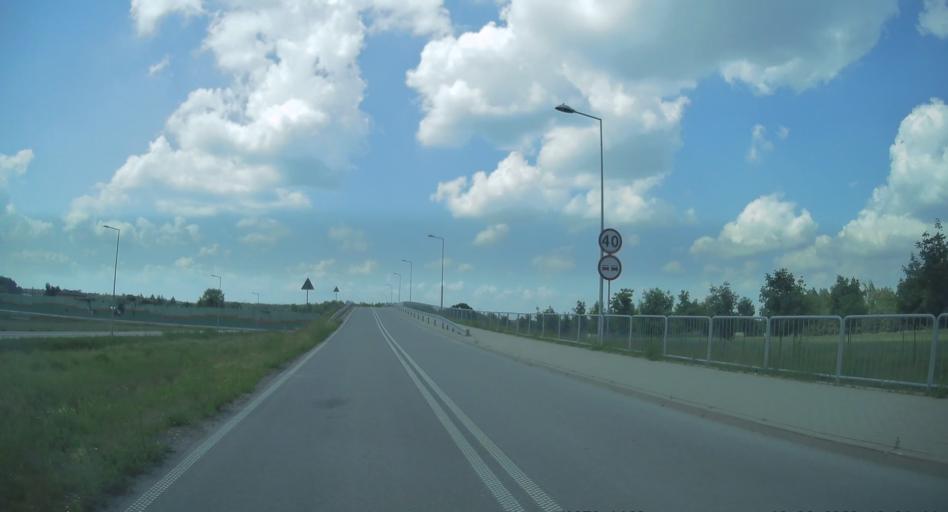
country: PL
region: Lodz Voivodeship
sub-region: Powiat tomaszowski
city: Czerniewice
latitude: 51.6931
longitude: 20.2142
